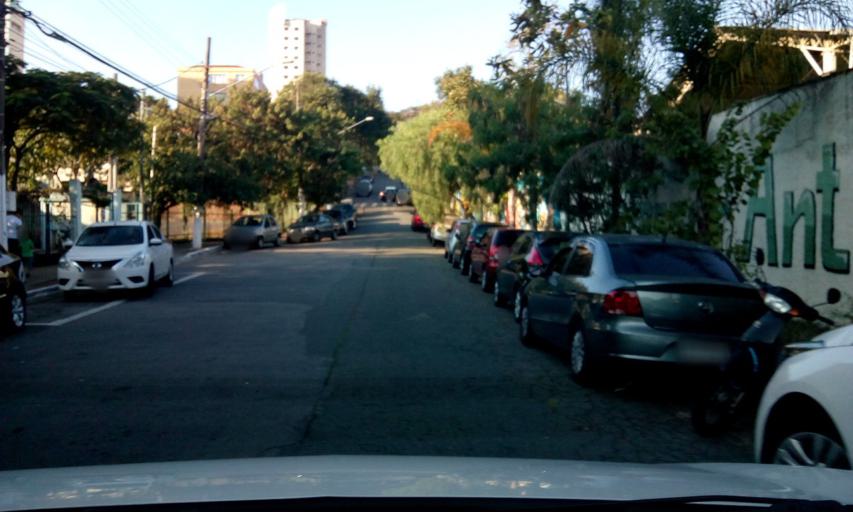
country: BR
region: Sao Paulo
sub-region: Sao Paulo
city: Sao Paulo
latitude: -23.4928
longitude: -46.6165
